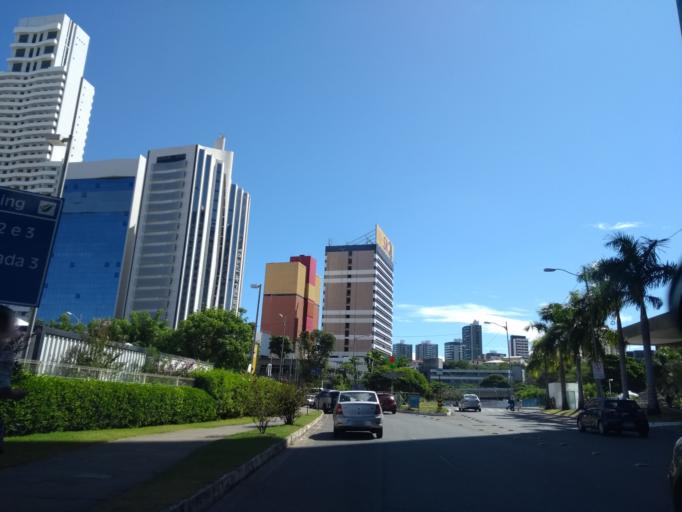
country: BR
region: Bahia
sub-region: Salvador
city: Salvador
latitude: -12.9775
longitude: -38.4570
